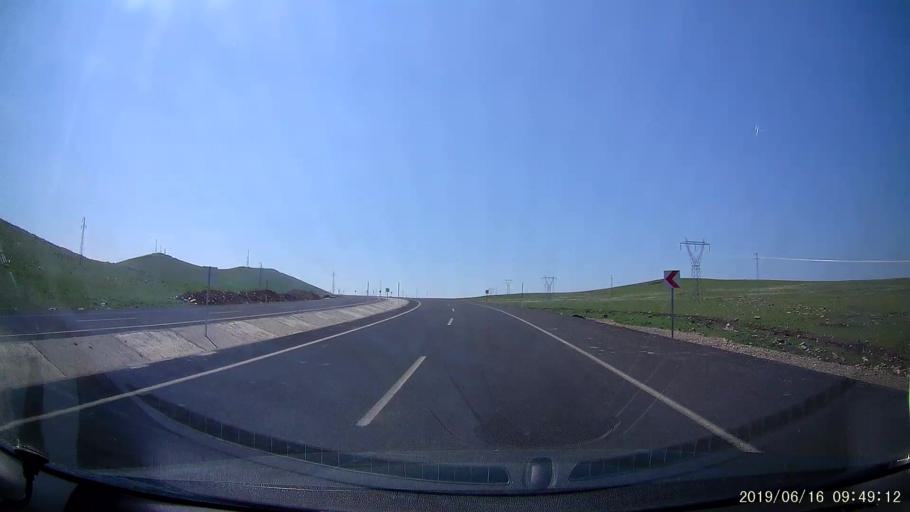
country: TR
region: Kars
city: Digor
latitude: 40.4241
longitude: 43.3567
